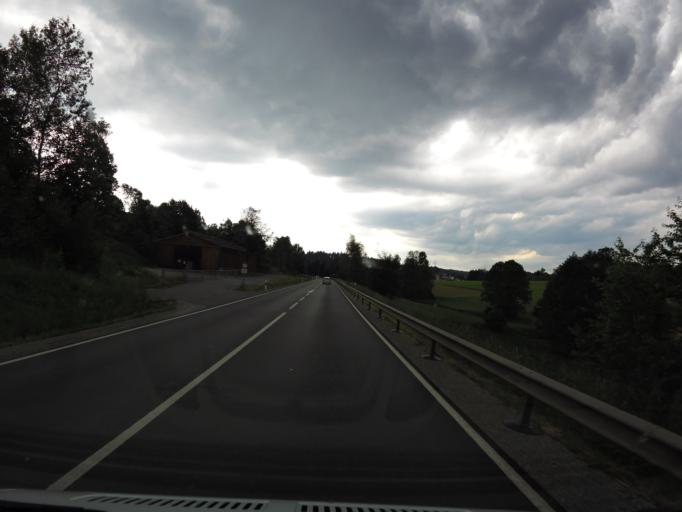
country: DE
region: Bavaria
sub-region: Lower Bavaria
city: Aicha vorm Wald
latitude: 48.6805
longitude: 13.2934
